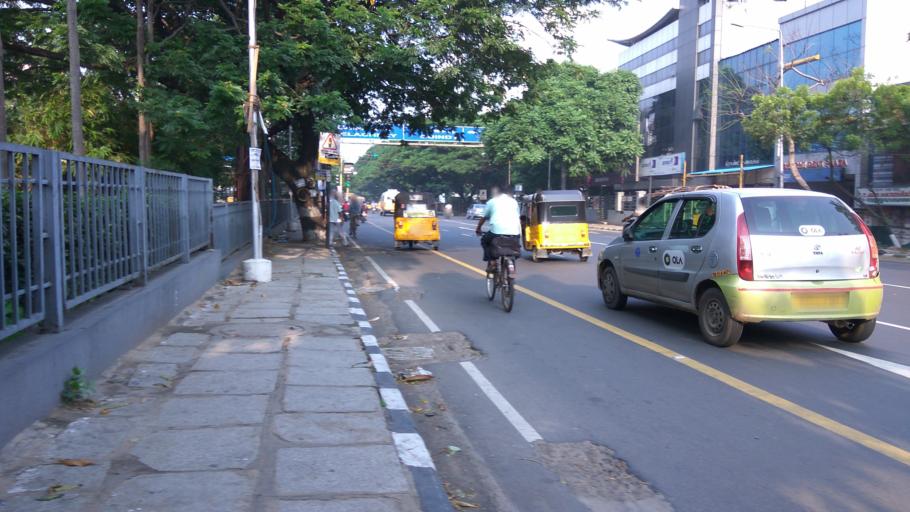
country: IN
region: Tamil Nadu
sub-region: Kancheepuram
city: Alandur
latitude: 13.0110
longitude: 80.2238
